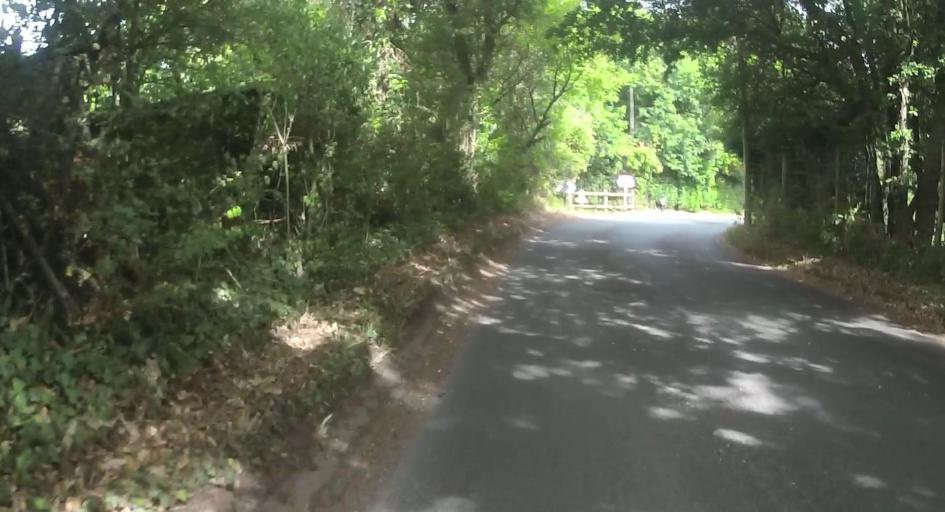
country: GB
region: England
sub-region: Dorset
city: Wool
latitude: 50.6751
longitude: -2.1800
